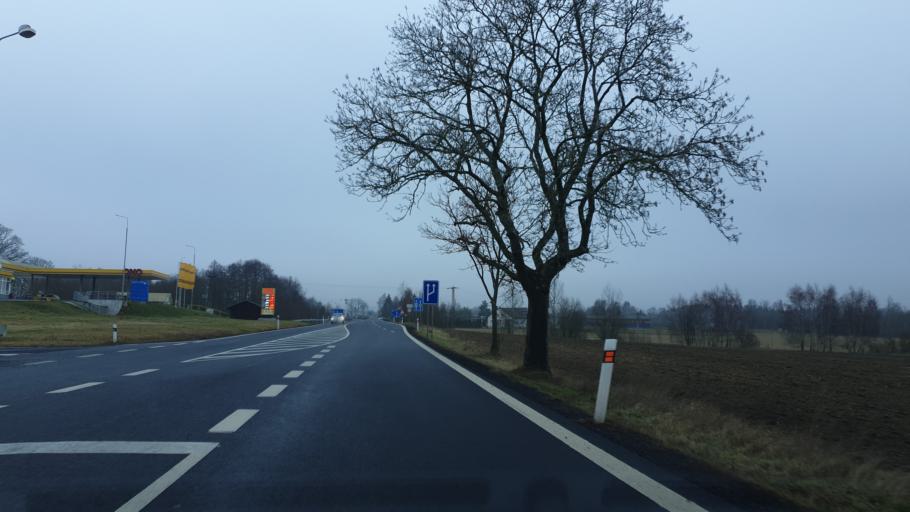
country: CZ
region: Karlovarsky
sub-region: Okres Cheb
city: Skalna
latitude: 50.1623
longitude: 12.3197
